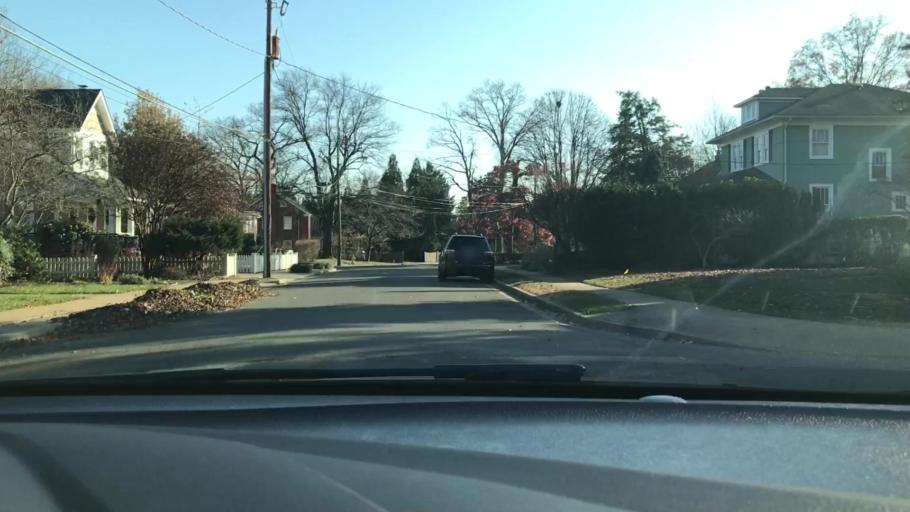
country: US
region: Virginia
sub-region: Arlington County
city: Arlington
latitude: 38.8765
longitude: -77.0967
